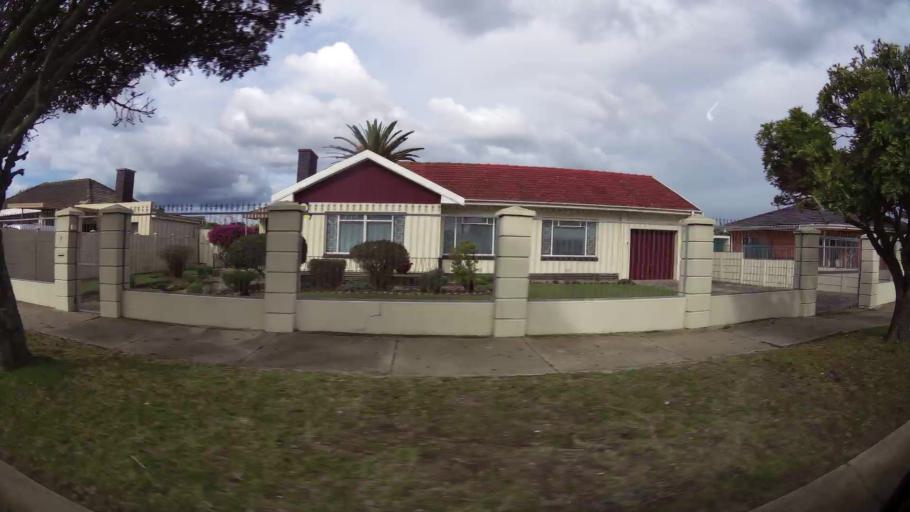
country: ZA
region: Eastern Cape
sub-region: Nelson Mandela Bay Metropolitan Municipality
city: Port Elizabeth
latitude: -33.9353
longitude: 25.5121
